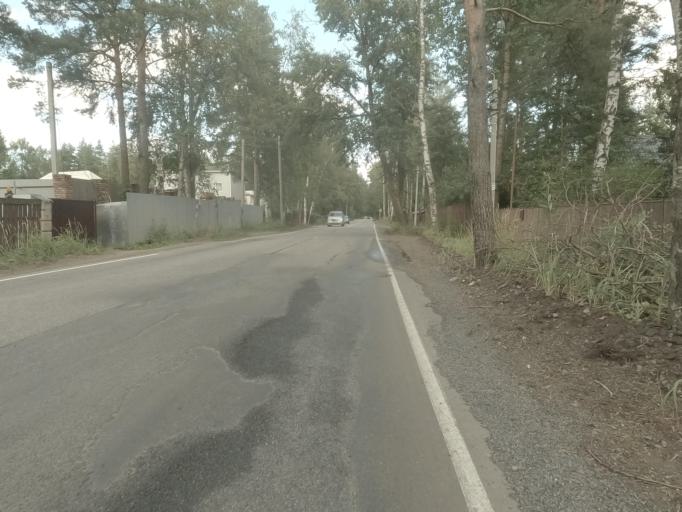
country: RU
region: Leningrad
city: Vsevolozhsk
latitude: 60.0208
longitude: 30.6879
